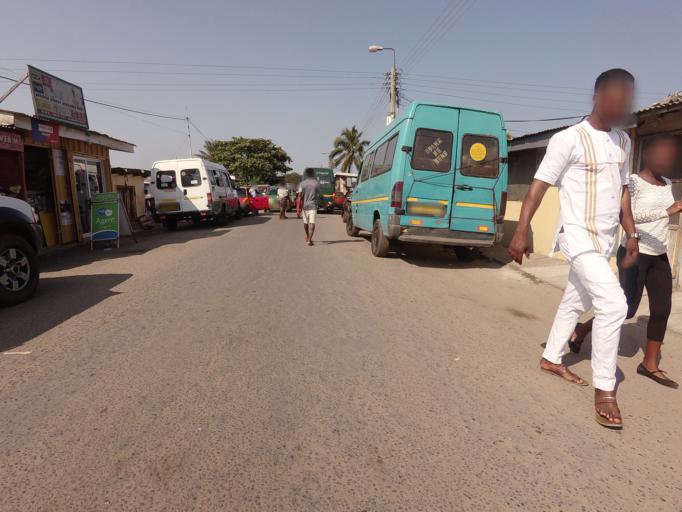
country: GH
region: Greater Accra
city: Teshi Old Town
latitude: 5.5784
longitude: -0.1048
